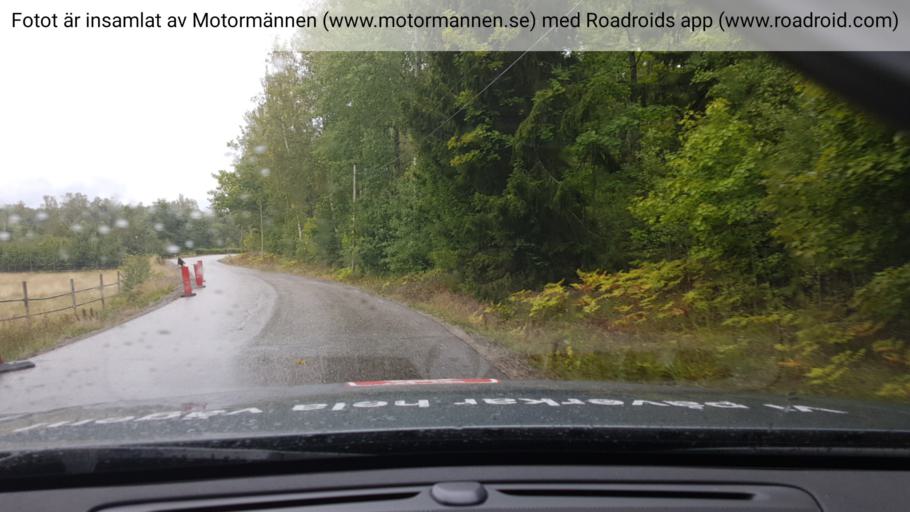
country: SE
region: Stockholm
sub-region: Nynashamns Kommun
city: Osmo
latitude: 59.0763
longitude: 17.8784
